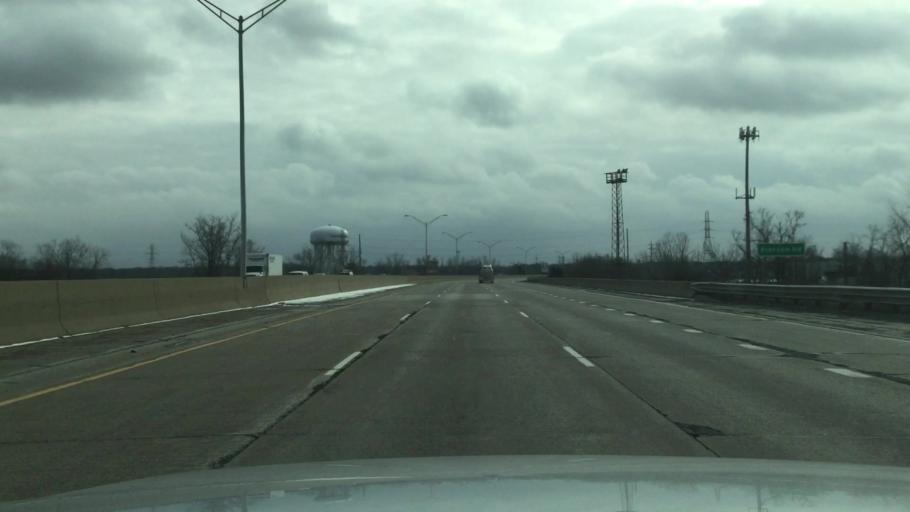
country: US
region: Michigan
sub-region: Genesee County
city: Beecher
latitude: 43.0619
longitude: -83.6784
